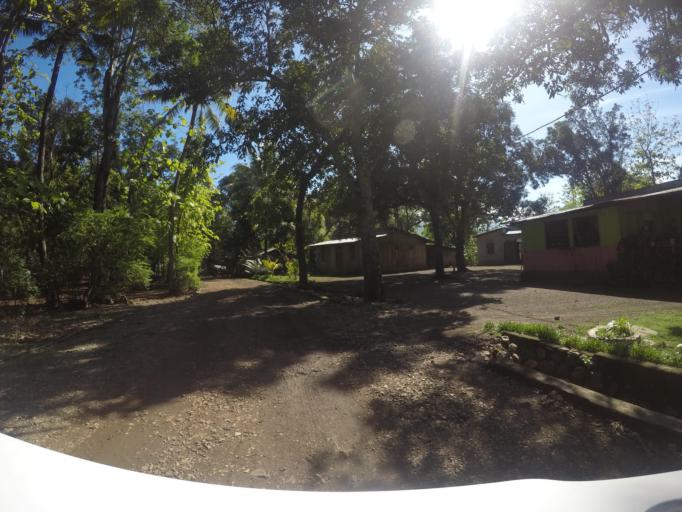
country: TL
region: Bobonaro
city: Maliana
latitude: -8.9905
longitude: 125.2071
